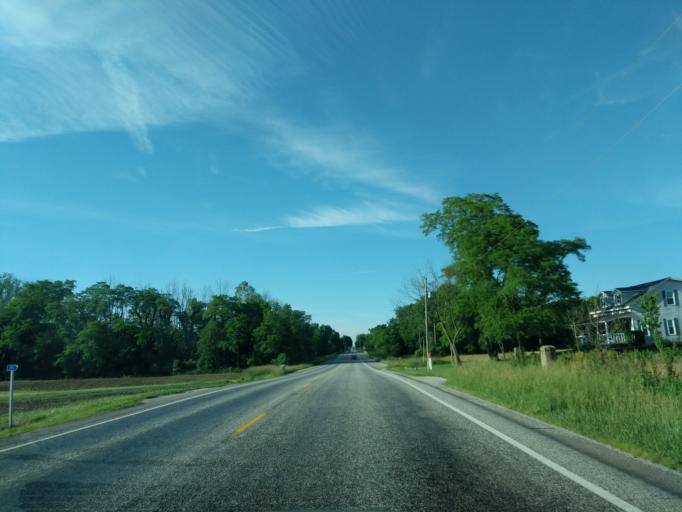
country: US
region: Indiana
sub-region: Madison County
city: Ingalls
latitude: 39.9117
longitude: -85.7709
